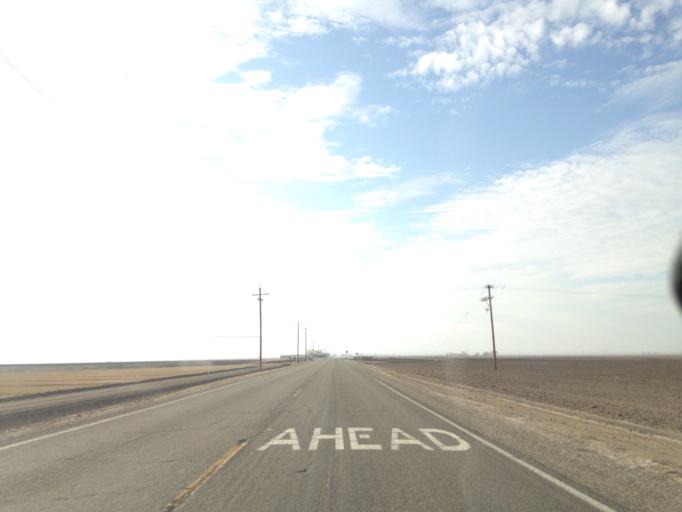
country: US
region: California
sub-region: Kern County
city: Buttonwillow
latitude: 35.4417
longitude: -119.5474
